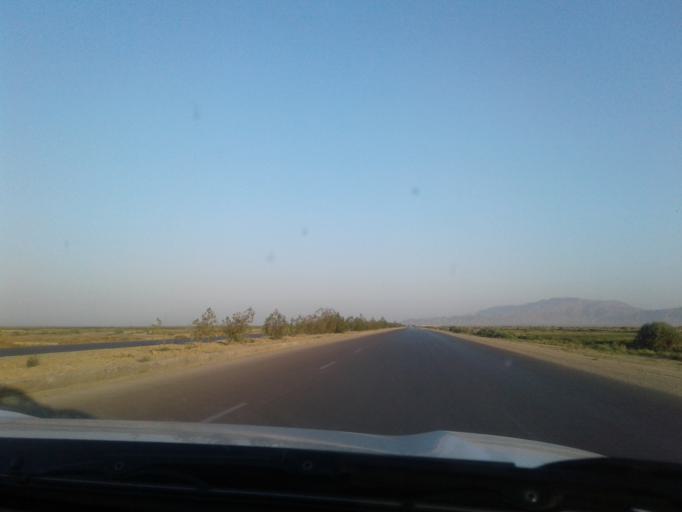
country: TM
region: Ahal
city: Baharly
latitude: 38.3652
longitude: 57.5255
